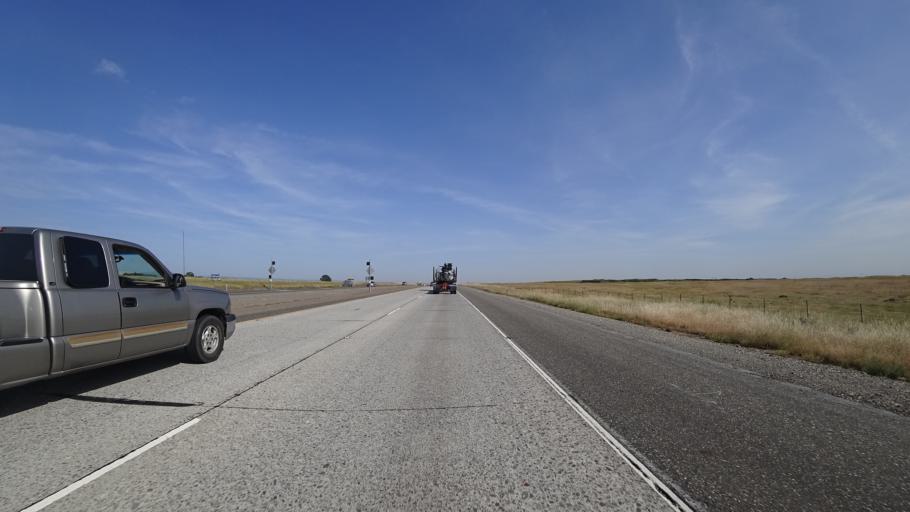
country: US
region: California
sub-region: Butte County
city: Durham
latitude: 39.6641
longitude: -121.7419
